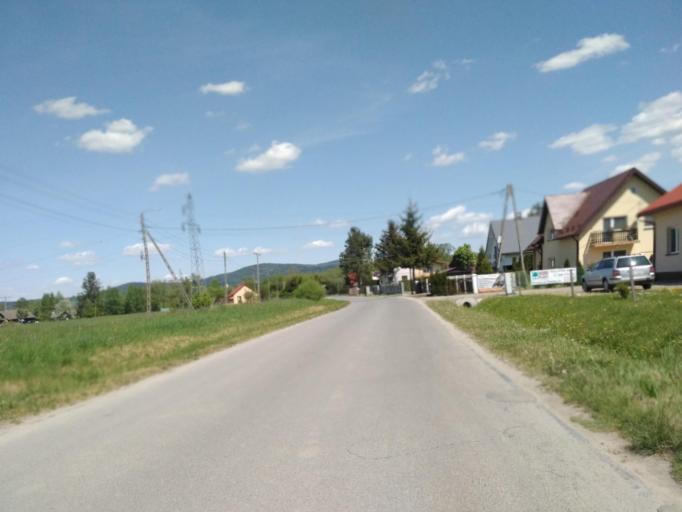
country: PL
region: Subcarpathian Voivodeship
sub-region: Powiat krosnienski
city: Odrzykon
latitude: 49.7235
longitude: 21.7209
